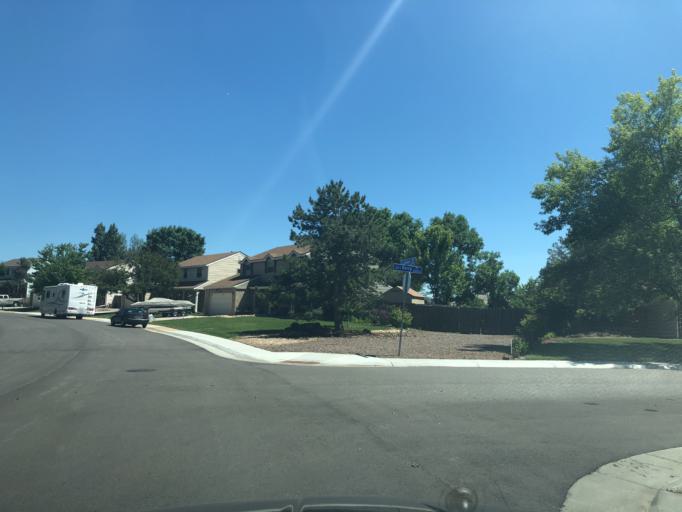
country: US
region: Colorado
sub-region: Arapahoe County
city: Dove Valley
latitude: 39.6158
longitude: -104.7873
